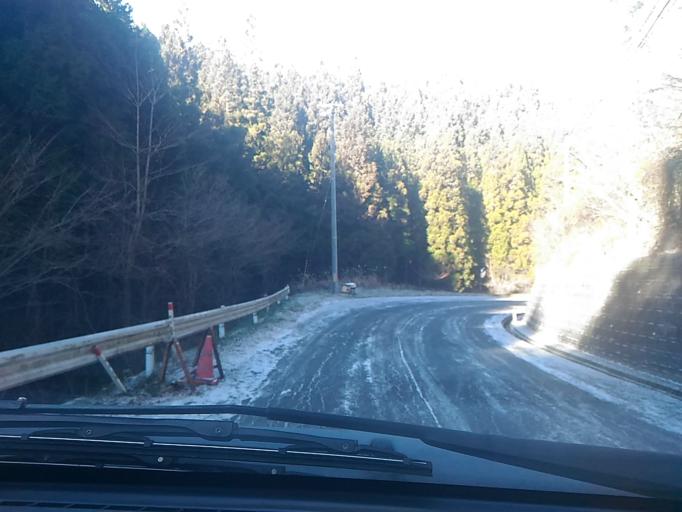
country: JP
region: Fukushima
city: Ishikawa
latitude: 36.9664
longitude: 140.5428
